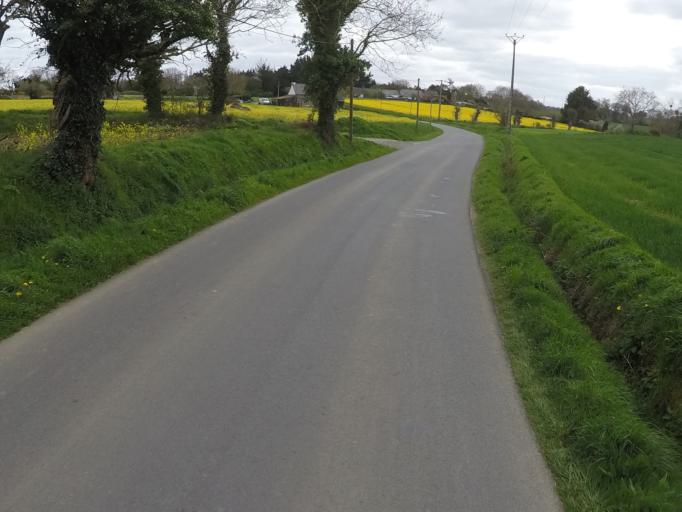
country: FR
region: Brittany
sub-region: Departement des Cotes-d'Armor
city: Plouha
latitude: 48.6662
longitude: -2.9210
